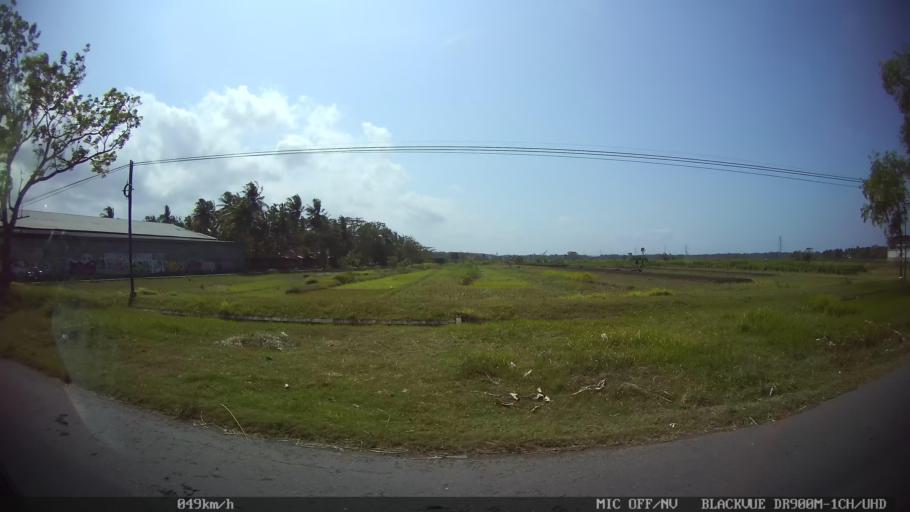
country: ID
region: Daerah Istimewa Yogyakarta
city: Srandakan
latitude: -7.8968
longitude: 110.1525
